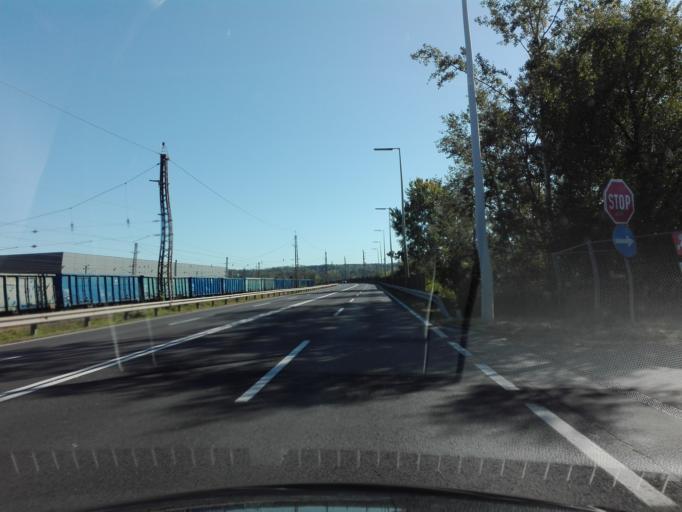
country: AT
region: Upper Austria
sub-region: Politischer Bezirk Urfahr-Umgebung
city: Steyregg
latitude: 48.2631
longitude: 14.3237
